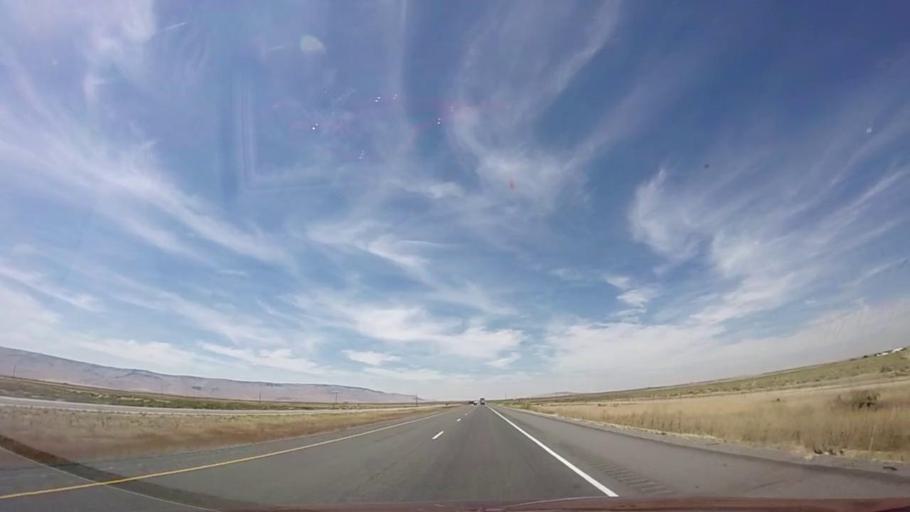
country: US
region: Idaho
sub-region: Minidoka County
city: Rupert
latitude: 42.4325
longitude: -113.3394
